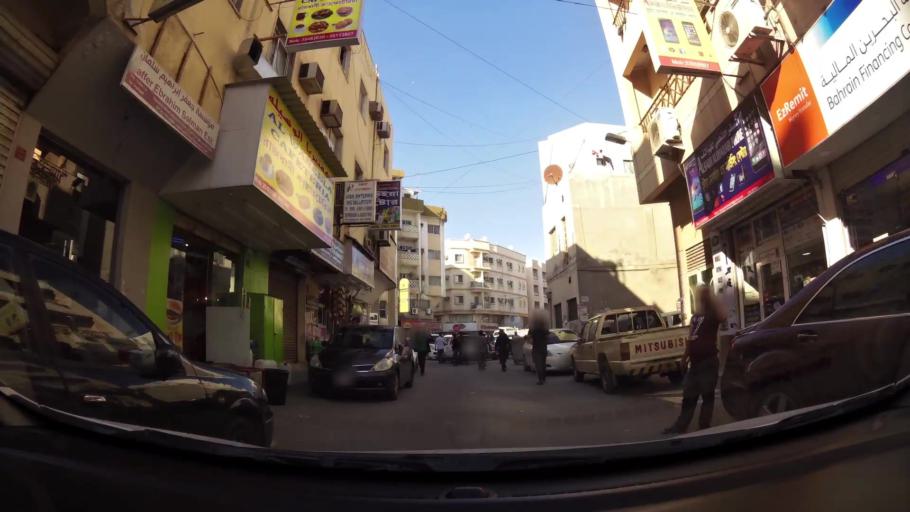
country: BH
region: Manama
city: Manama
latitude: 26.2274
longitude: 50.5723
